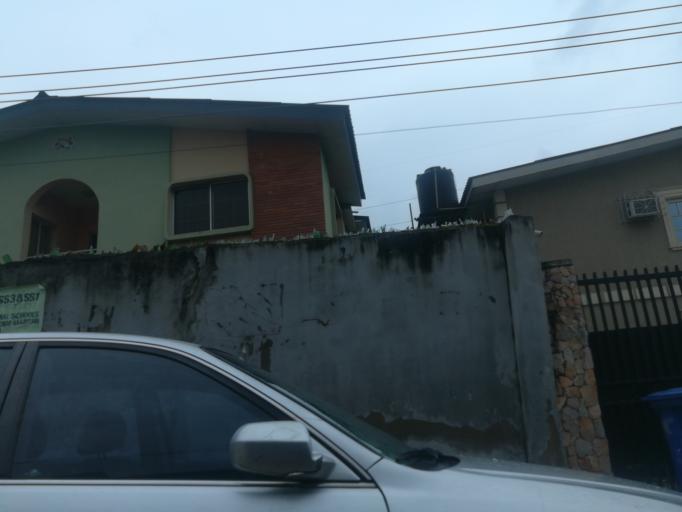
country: NG
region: Lagos
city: Ojota
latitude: 6.5739
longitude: 3.3723
